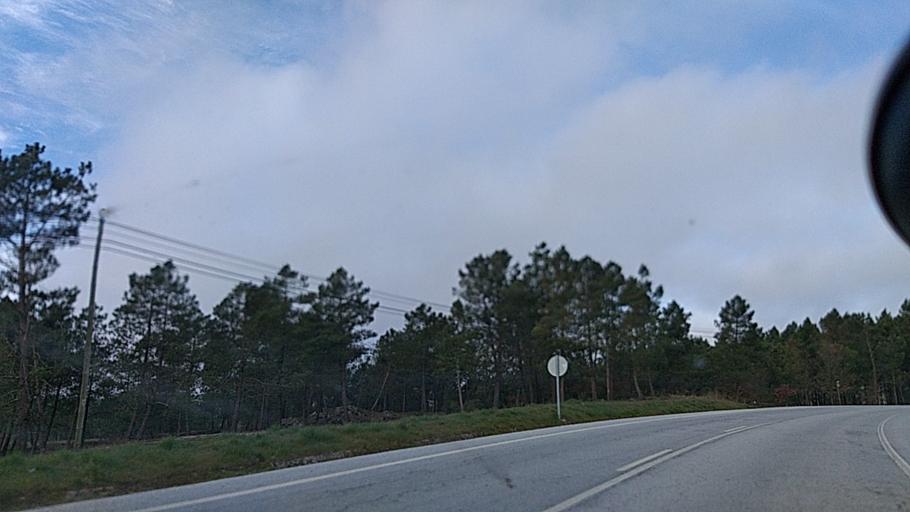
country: PT
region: Guarda
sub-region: Aguiar da Beira
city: Aguiar da Beira
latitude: 40.8084
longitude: -7.5312
